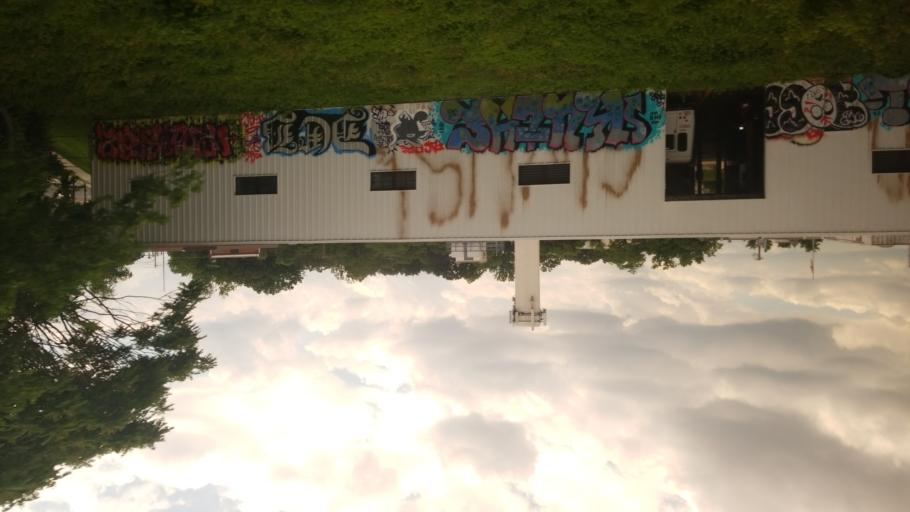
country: US
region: Maryland
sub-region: Montgomery County
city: Takoma Park
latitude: 38.9636
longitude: -77.0095
